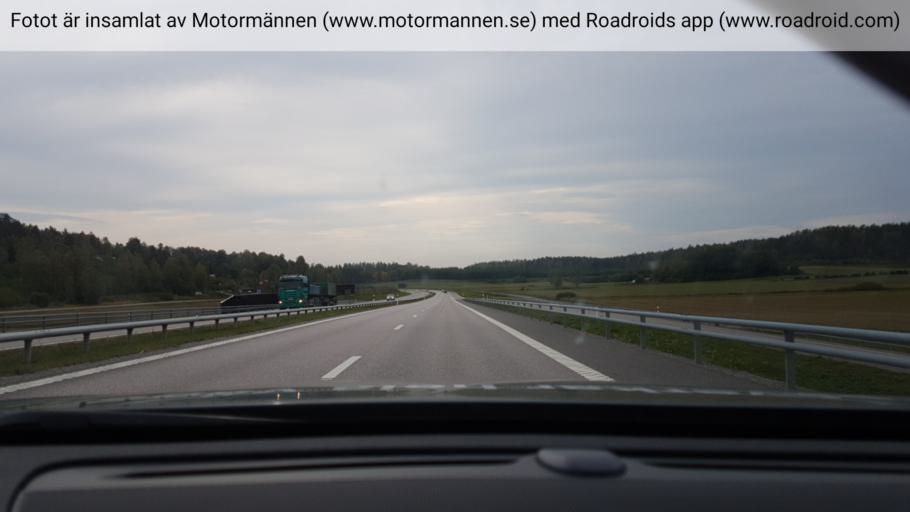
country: SE
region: Stockholm
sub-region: Nynashamns Kommun
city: Osmo
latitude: 58.9575
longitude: 17.9039
